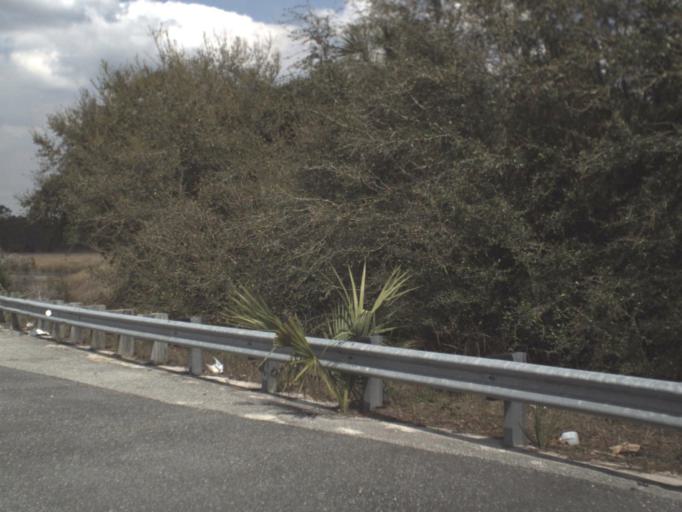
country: US
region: Florida
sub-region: Franklin County
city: Eastpoint
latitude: 29.8204
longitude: -84.8508
